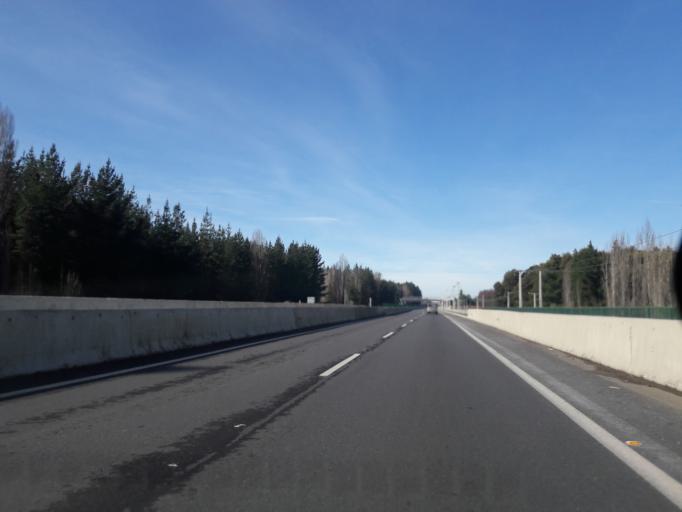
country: CL
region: Biobio
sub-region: Provincia de Biobio
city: Yumbel
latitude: -37.0090
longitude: -72.5230
